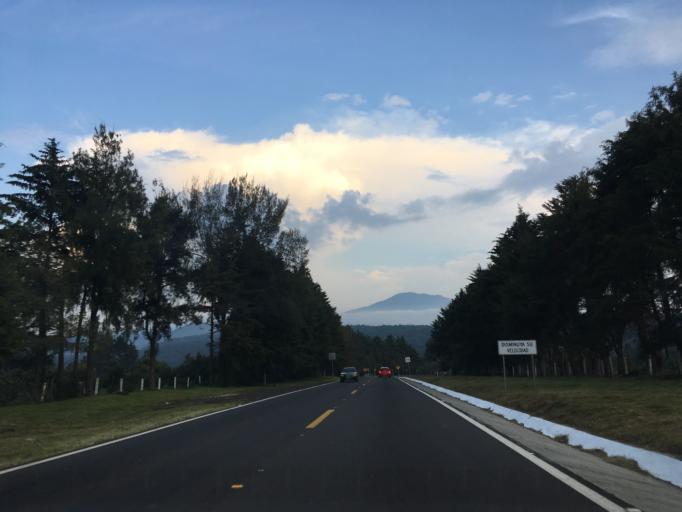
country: MX
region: Michoacan
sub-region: Patzcuaro
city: Santa Maria Huiramangaro (San Juan Tumbio)
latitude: 19.4906
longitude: -101.7409
